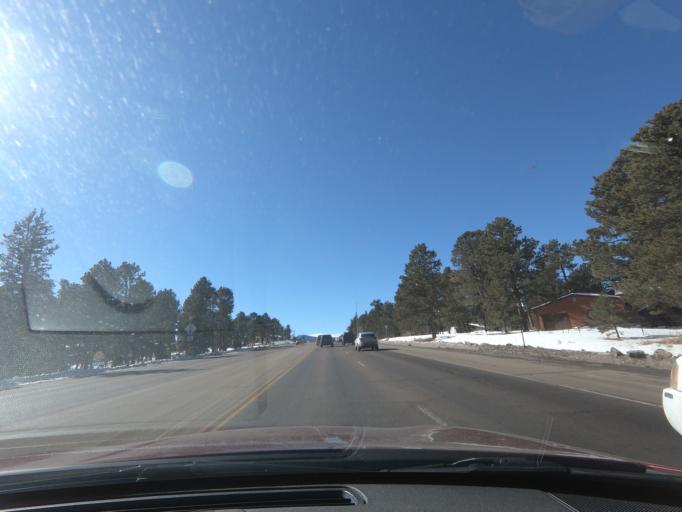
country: US
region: Colorado
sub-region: Teller County
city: Woodland Park
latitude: 38.9737
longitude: -105.0776
